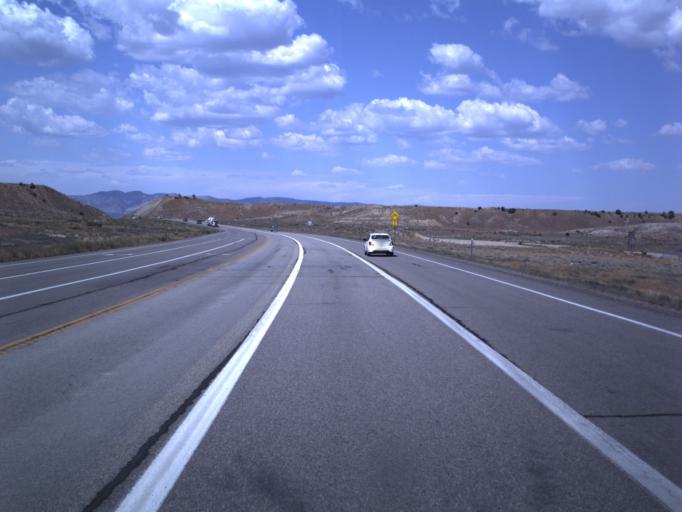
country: US
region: Utah
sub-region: Carbon County
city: Price
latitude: 39.5361
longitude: -110.8156
